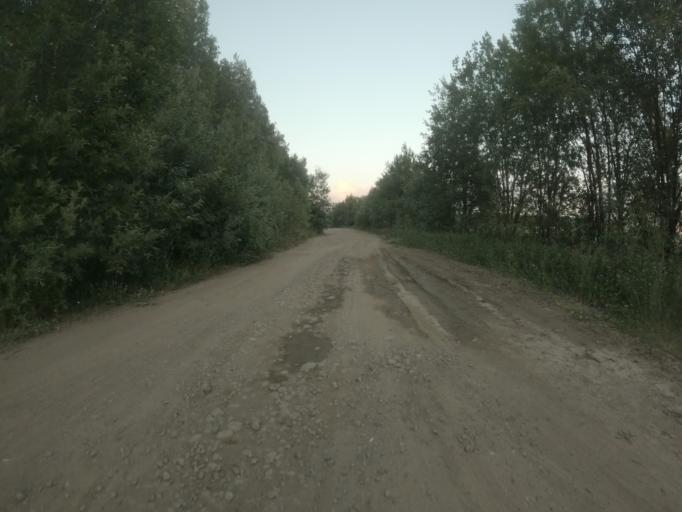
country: RU
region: Leningrad
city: Yanino Vtoroye
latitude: 59.9585
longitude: 30.5582
